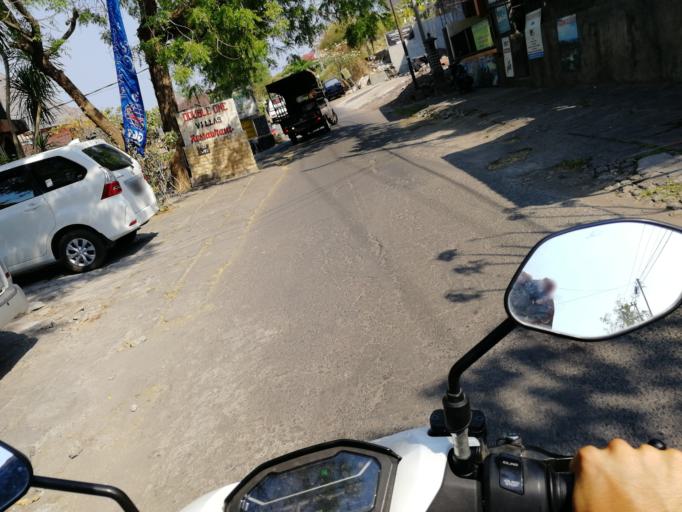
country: ID
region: Bali
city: Biaslantang Kaler
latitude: -8.3465
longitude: 115.6778
